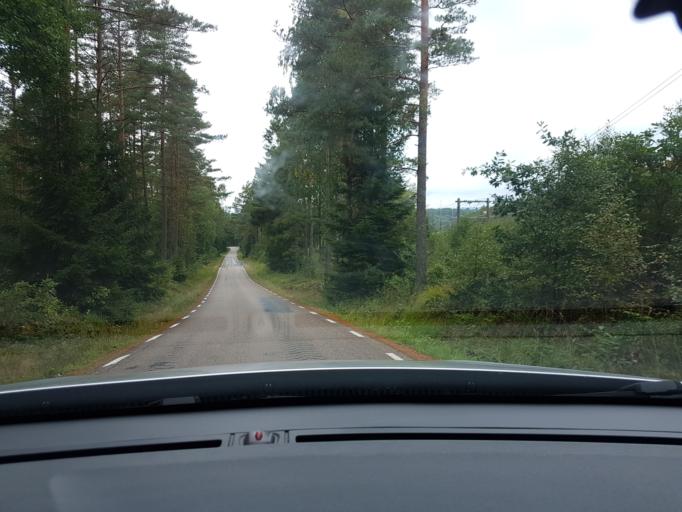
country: SE
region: Vaestra Goetaland
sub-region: Ale Kommun
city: Alvangen
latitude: 57.9069
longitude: 12.1732
